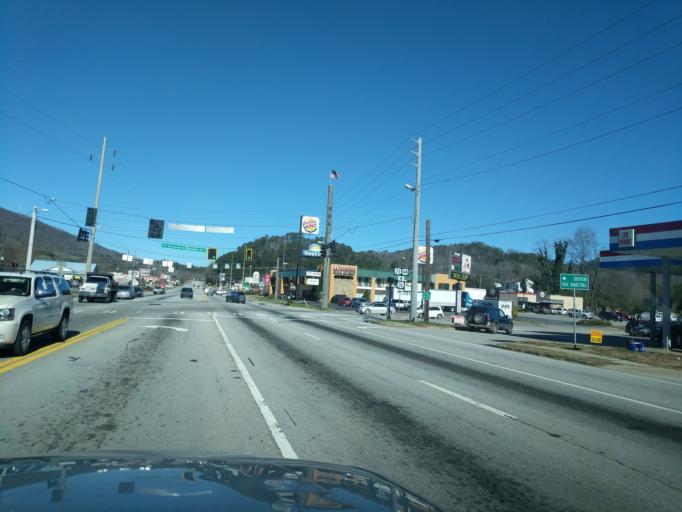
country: US
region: Georgia
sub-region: Rabun County
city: Clayton
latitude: 34.8768
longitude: -83.3974
